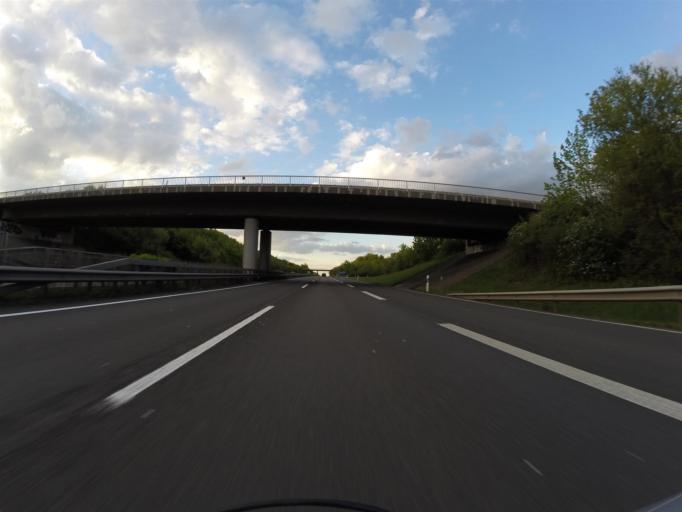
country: DE
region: Rheinland-Pfalz
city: Alzey
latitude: 49.7475
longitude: 8.0858
